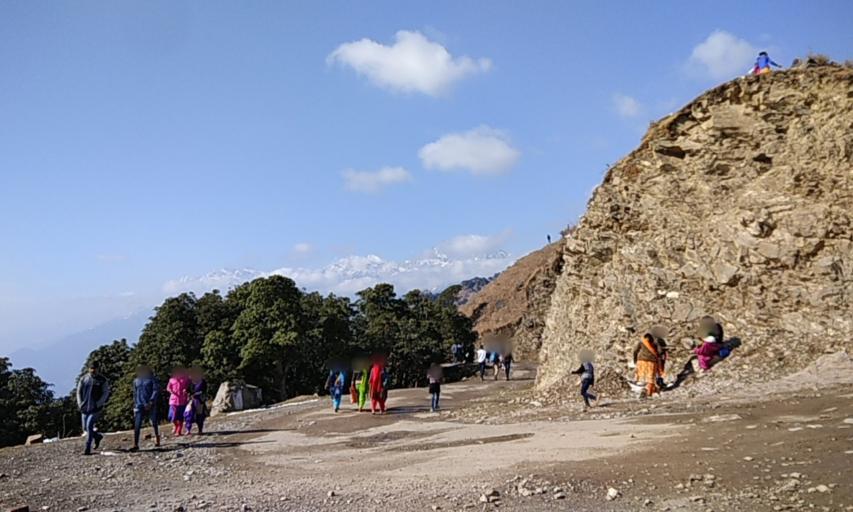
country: IN
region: Himachal Pradesh
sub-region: Mandi
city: Jogindarnagar
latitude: 32.0565
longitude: 76.7441
